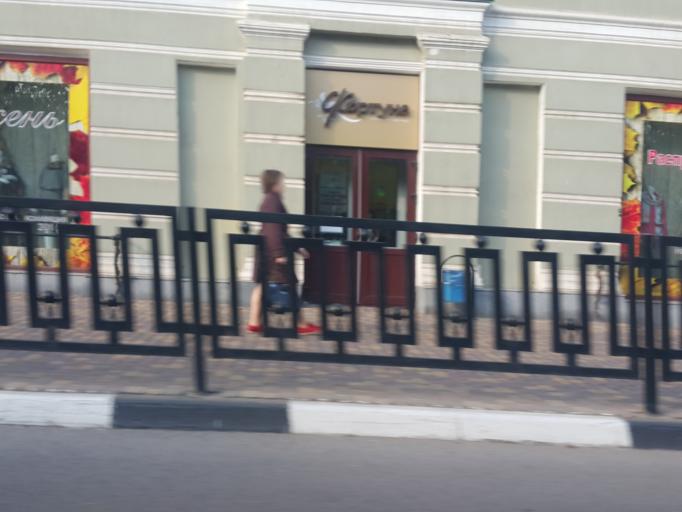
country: RU
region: Tambov
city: Tambov
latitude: 52.7225
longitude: 41.4514
